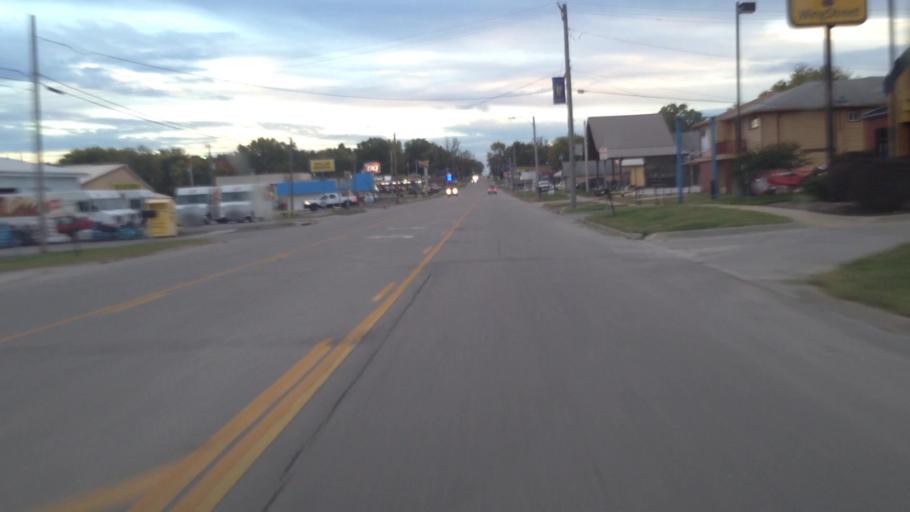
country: US
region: Kansas
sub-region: Anderson County
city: Garnett
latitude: 38.2874
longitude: -95.2493
